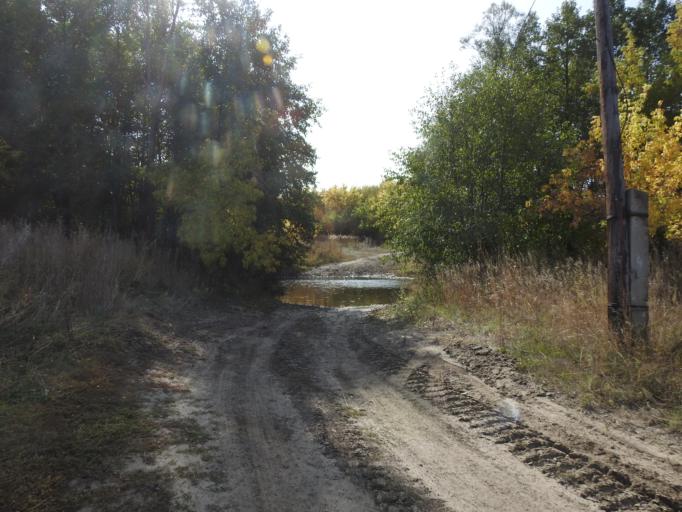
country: RU
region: Saratov
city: Baltay
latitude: 52.4991
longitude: 46.6608
